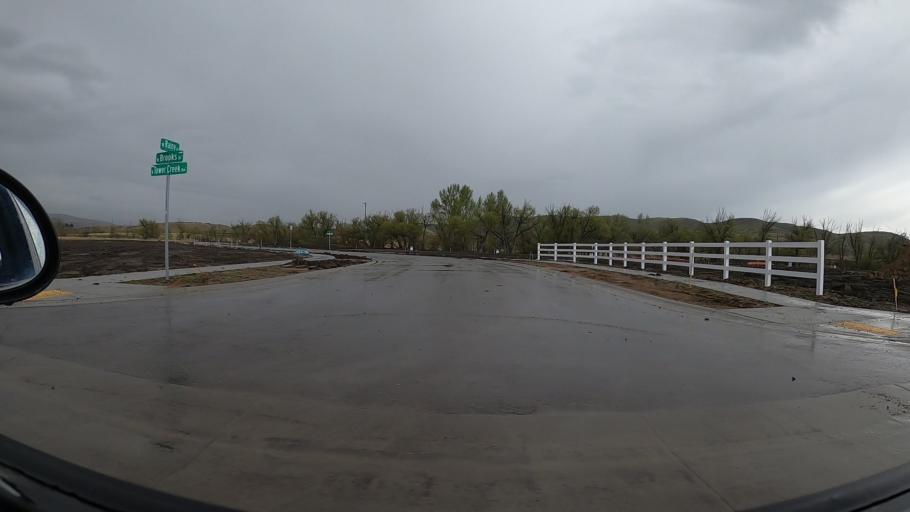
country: US
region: Idaho
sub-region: Ada County
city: Eagle
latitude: 43.7329
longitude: -116.2844
